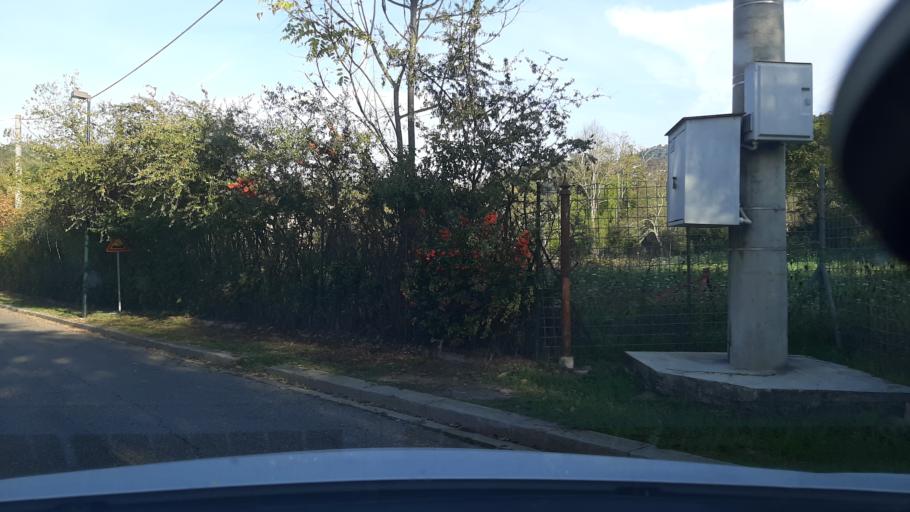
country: IT
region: Tuscany
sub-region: Province of Florence
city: Fiesole
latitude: 43.7892
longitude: 11.2948
